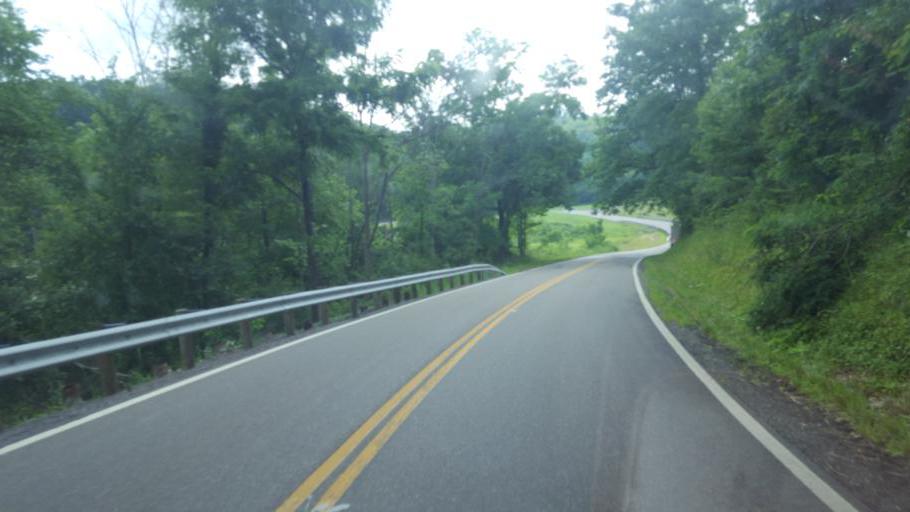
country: US
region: Ohio
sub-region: Columbiana County
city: Salineville
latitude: 40.5769
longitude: -80.8596
